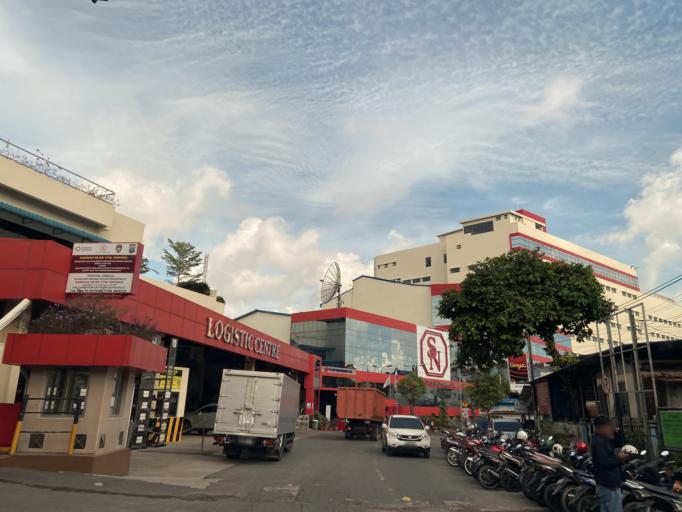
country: SG
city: Singapore
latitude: 1.1401
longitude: 104.0191
